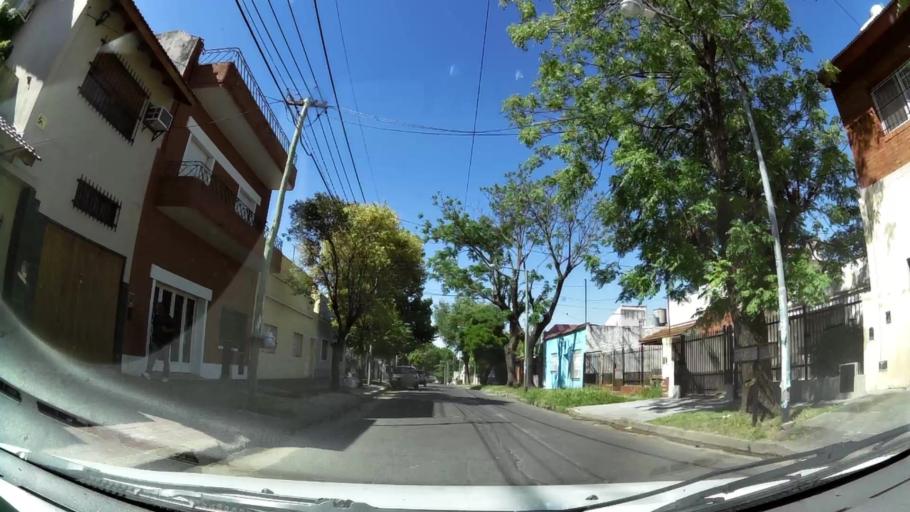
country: AR
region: Buenos Aires
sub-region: Partido de General San Martin
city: General San Martin
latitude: -34.5519
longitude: -58.5672
